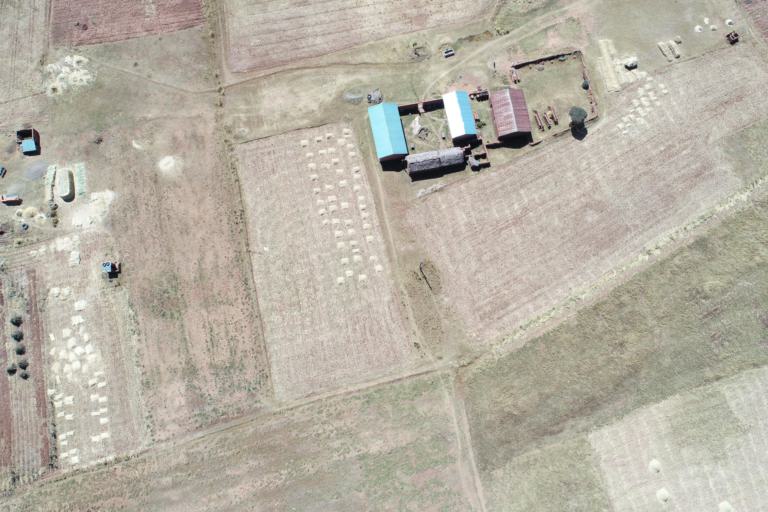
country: BO
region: La Paz
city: Tiahuanaco
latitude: -16.5893
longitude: -68.7694
